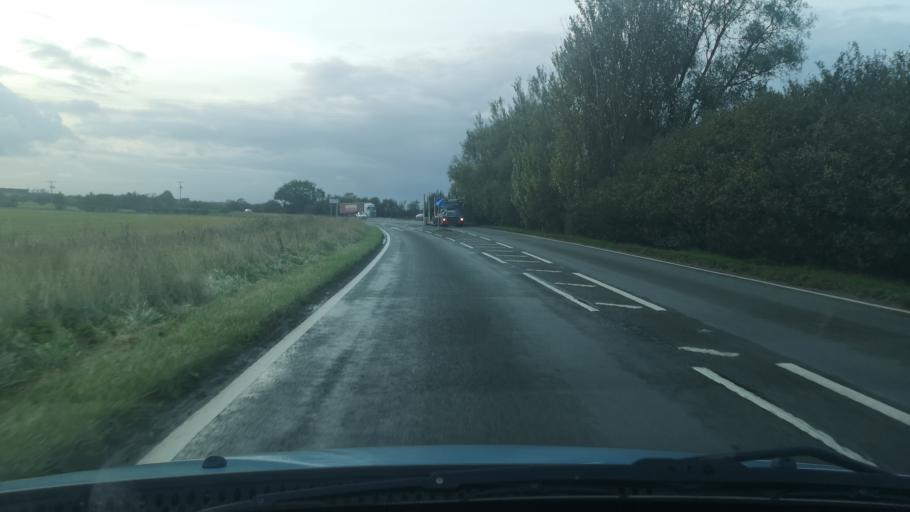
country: GB
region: England
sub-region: Doncaster
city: Hatfield
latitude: 53.5933
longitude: -0.9454
